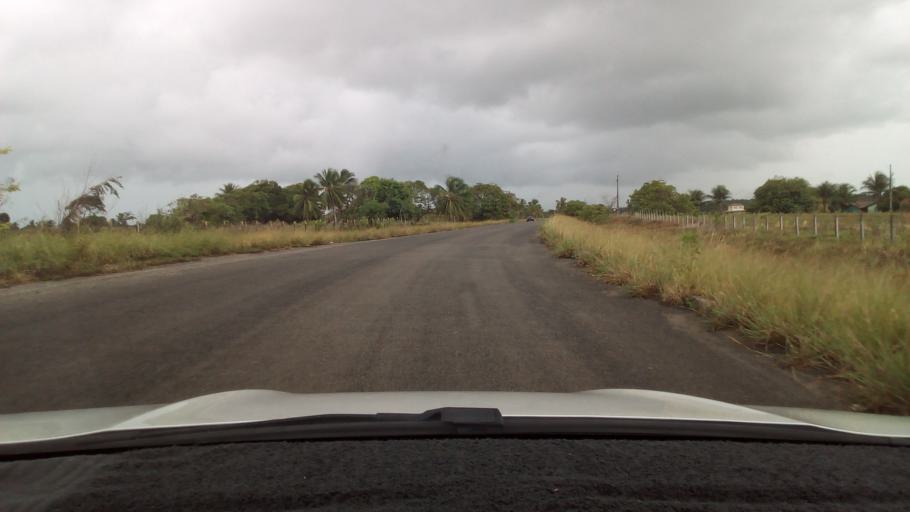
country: BR
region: Paraiba
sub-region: Pitimbu
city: Pitimbu
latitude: -7.4074
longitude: -34.8152
